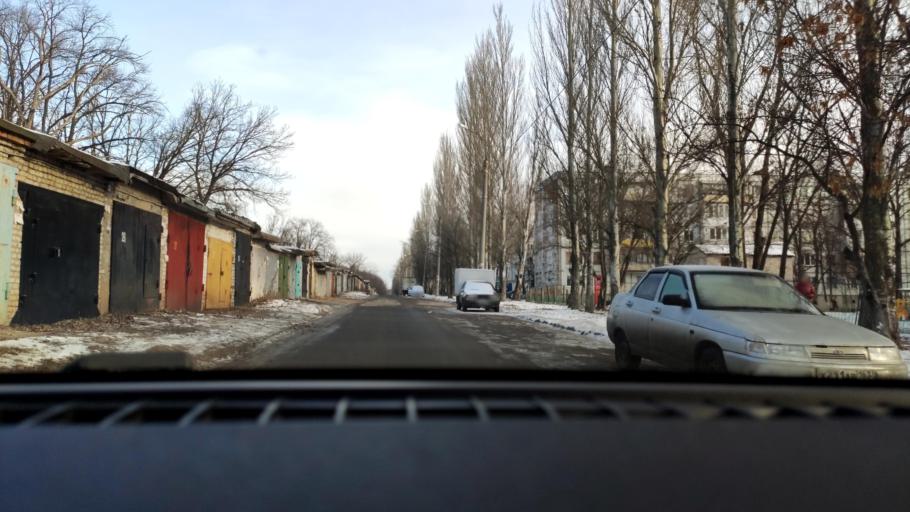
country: RU
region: Samara
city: Petra-Dubrava
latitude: 53.3036
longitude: 50.2676
